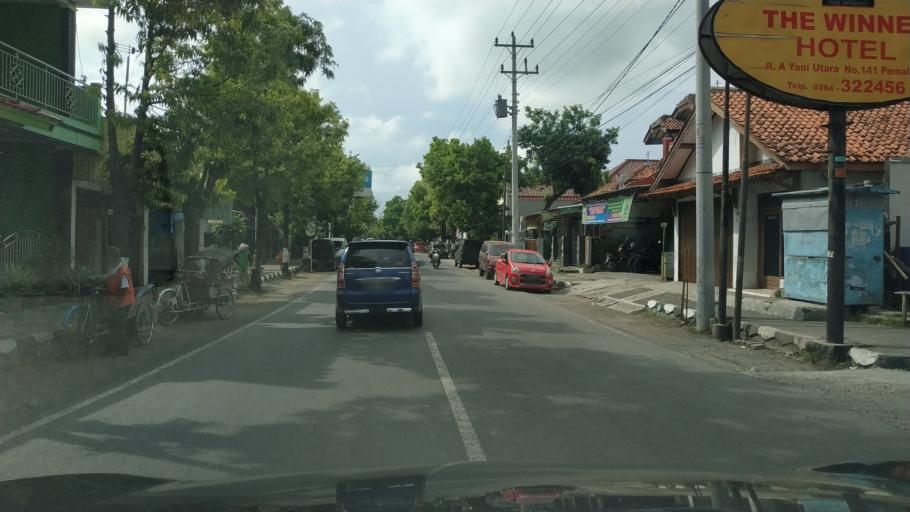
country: ID
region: Central Java
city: Pemalang
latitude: -6.8982
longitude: 109.3832
